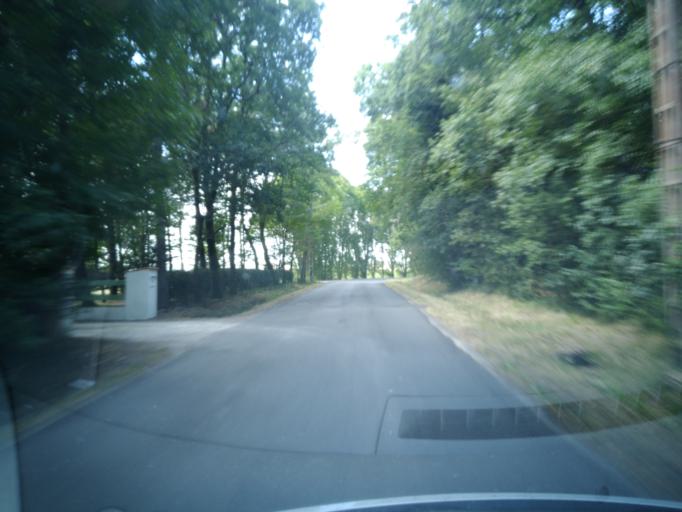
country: FR
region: Poitou-Charentes
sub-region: Departement de la Charente-Maritime
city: Breuillet
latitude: 45.6868
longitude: -1.0745
